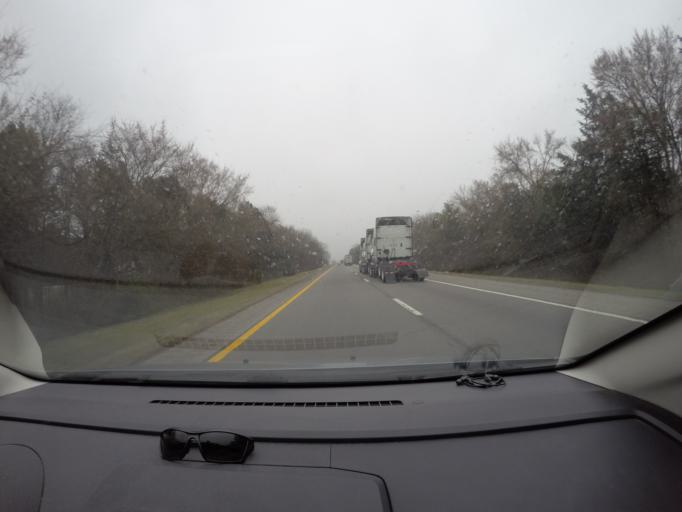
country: US
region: Tennessee
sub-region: Rutherford County
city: Plainview
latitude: 35.7370
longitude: -86.3326
